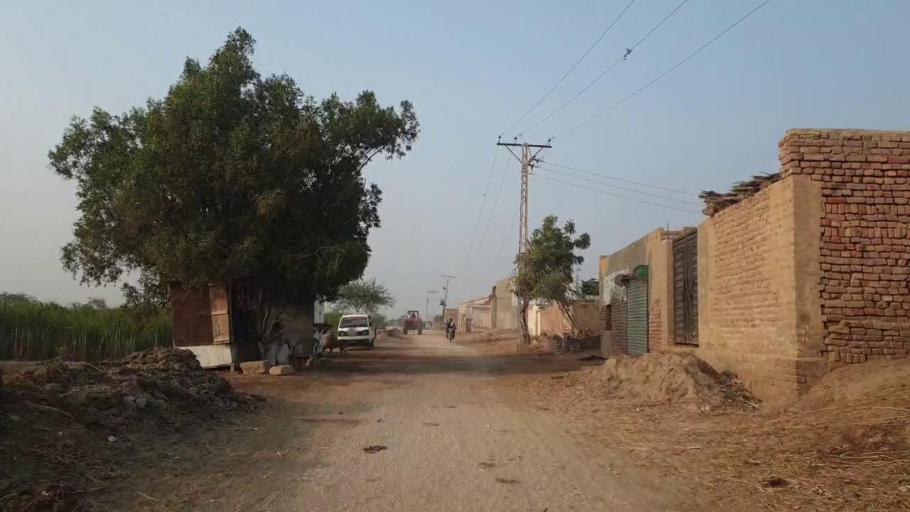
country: PK
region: Sindh
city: Tando Muhammad Khan
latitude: 25.0958
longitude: 68.4325
